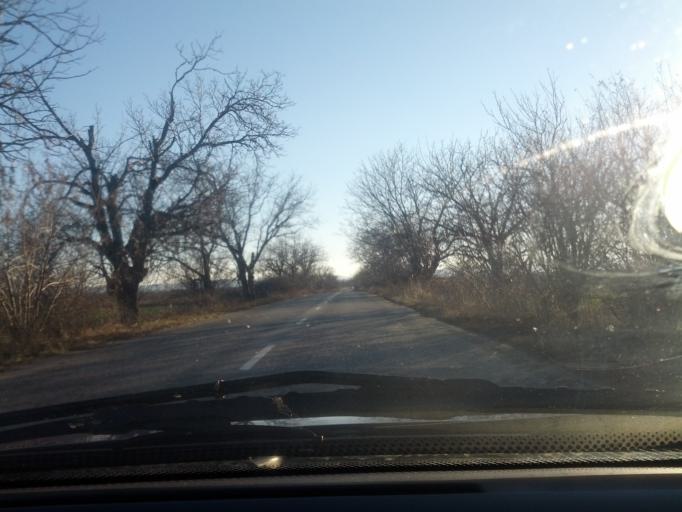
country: BG
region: Vratsa
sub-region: Obshtina Borovan
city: Borovan
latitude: 43.4845
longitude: 23.7948
